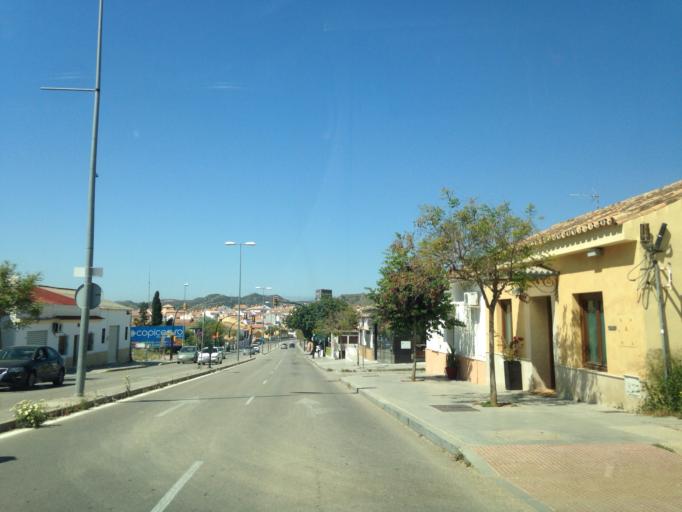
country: ES
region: Andalusia
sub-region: Provincia de Malaga
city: Malaga
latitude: 36.7402
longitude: -4.4832
